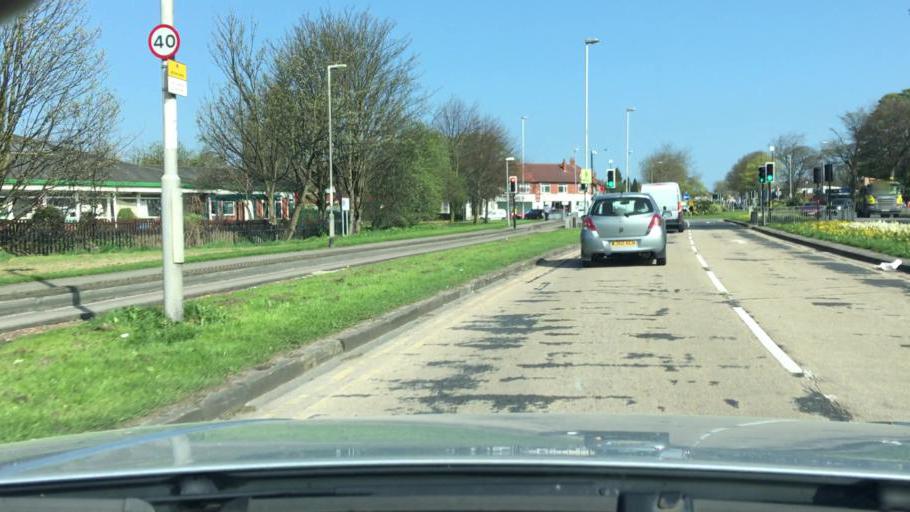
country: GB
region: England
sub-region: City and Borough of Leeds
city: Chapel Allerton
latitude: 53.8241
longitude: -1.5456
